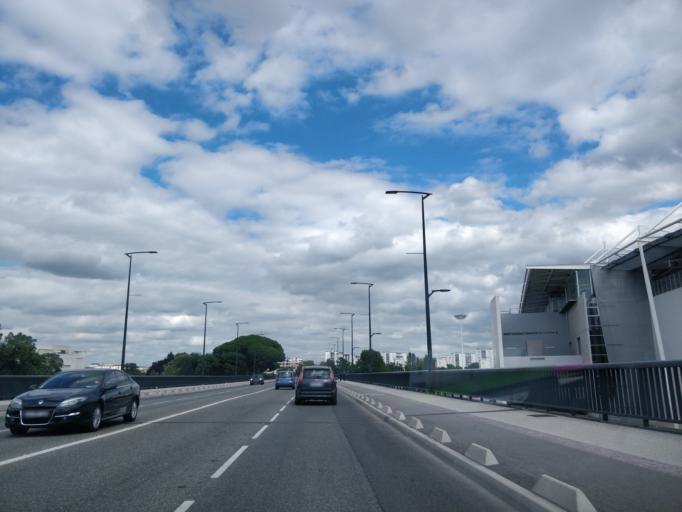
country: FR
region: Midi-Pyrenees
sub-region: Departement de la Haute-Garonne
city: Toulouse
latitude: 43.5844
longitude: 1.4333
